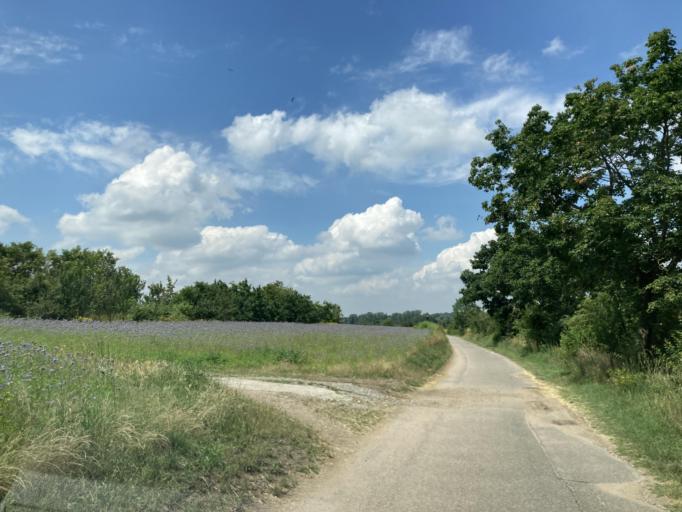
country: DE
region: Baden-Wuerttemberg
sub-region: Karlsruhe Region
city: Oberhausen-Rheinhausen
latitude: 49.2651
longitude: 8.4920
